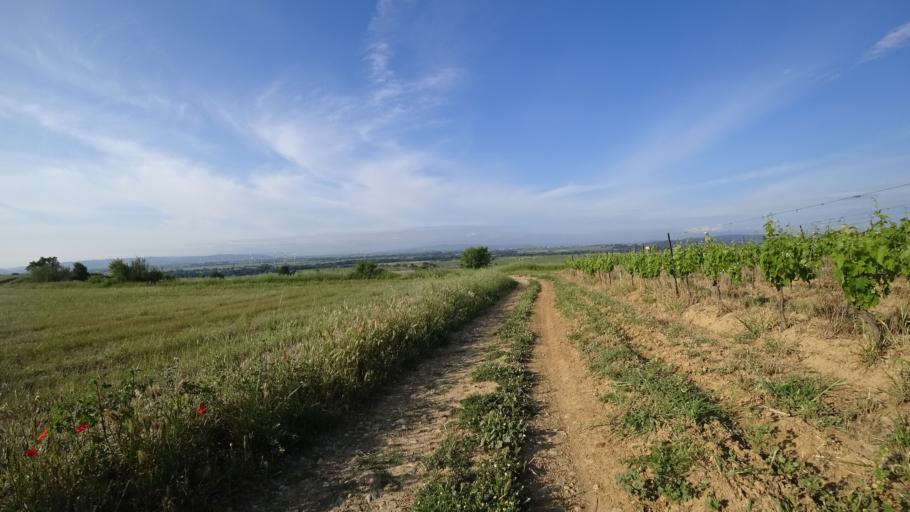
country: FR
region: Languedoc-Roussillon
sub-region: Departement de l'Aude
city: Canet
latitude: 43.2550
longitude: 2.8152
